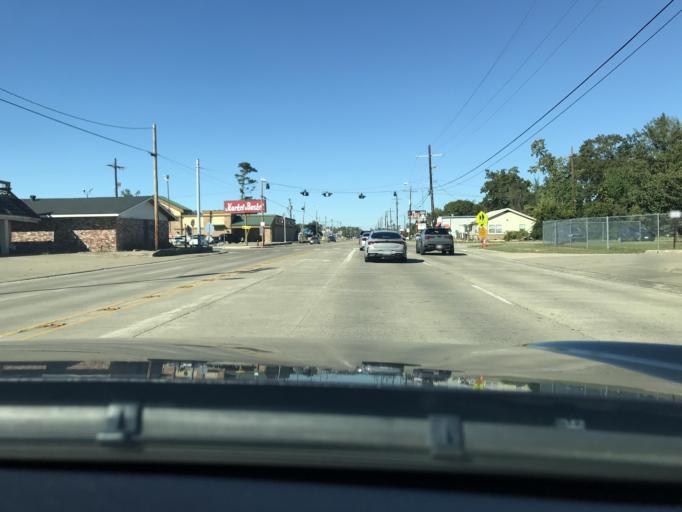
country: US
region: Louisiana
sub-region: Calcasieu Parish
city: Westlake
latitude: 30.2563
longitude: -93.2581
